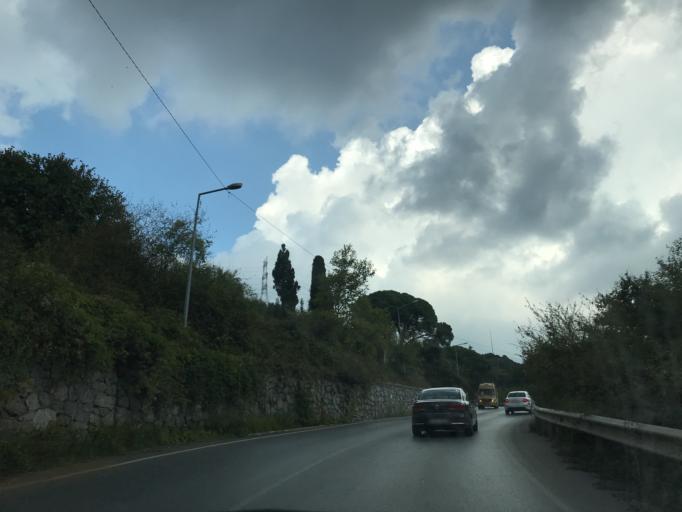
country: TR
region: Istanbul
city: Arikoey
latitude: 41.1833
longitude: 29.0445
